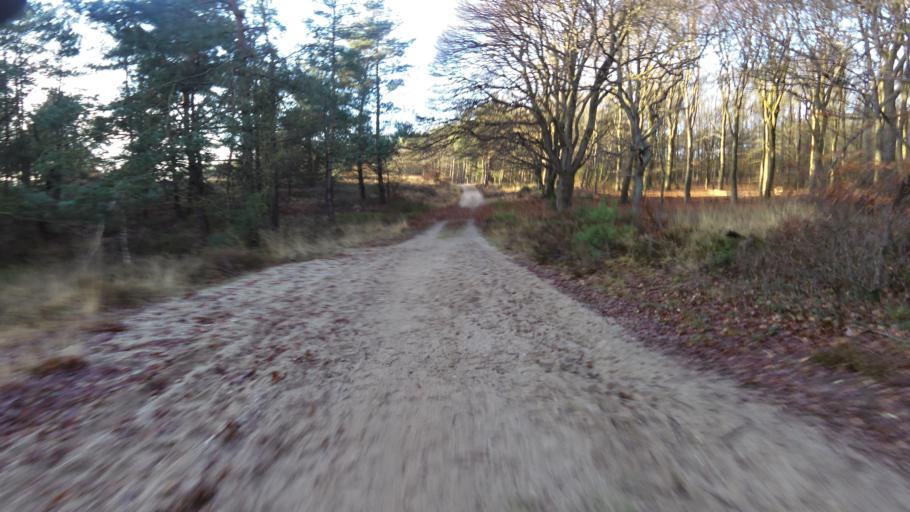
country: NL
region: Gelderland
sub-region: Gemeente Apeldoorn
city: Uddel
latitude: 52.2166
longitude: 5.8595
